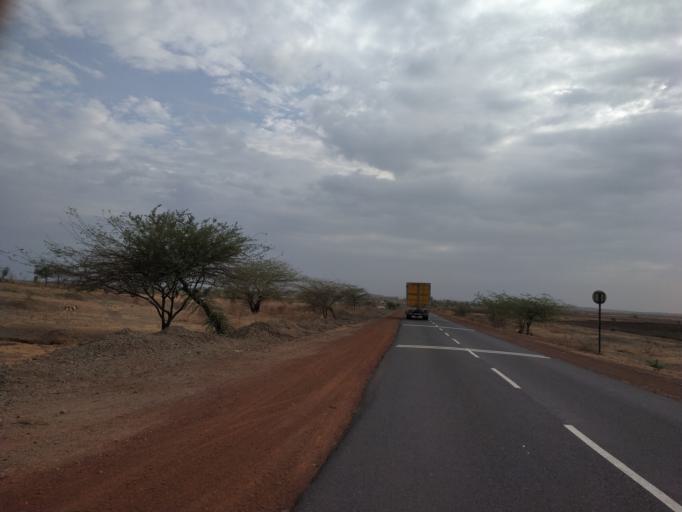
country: IN
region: Madhya Pradesh
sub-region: Shajapur
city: Agar
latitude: 23.6167
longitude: 75.9633
